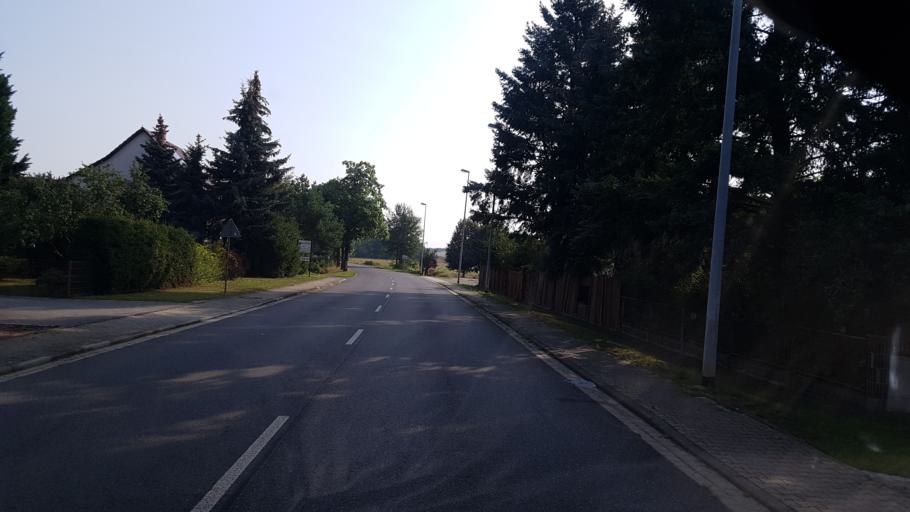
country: DE
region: Brandenburg
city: Drebkau
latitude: 51.6356
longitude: 14.1928
